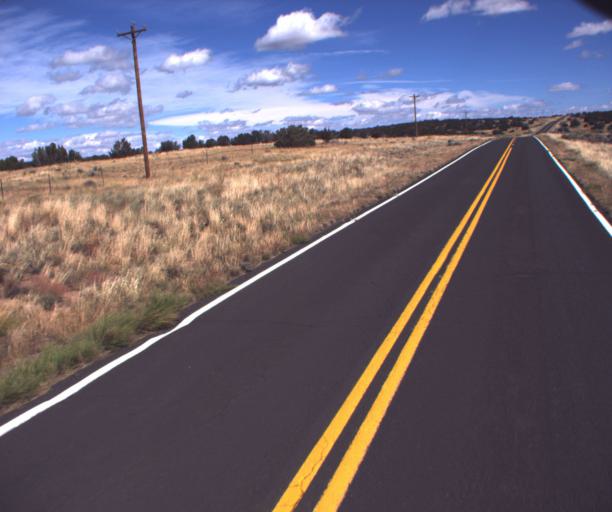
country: US
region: New Mexico
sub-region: McKinley County
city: Zuni Pueblo
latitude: 34.9815
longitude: -109.1269
